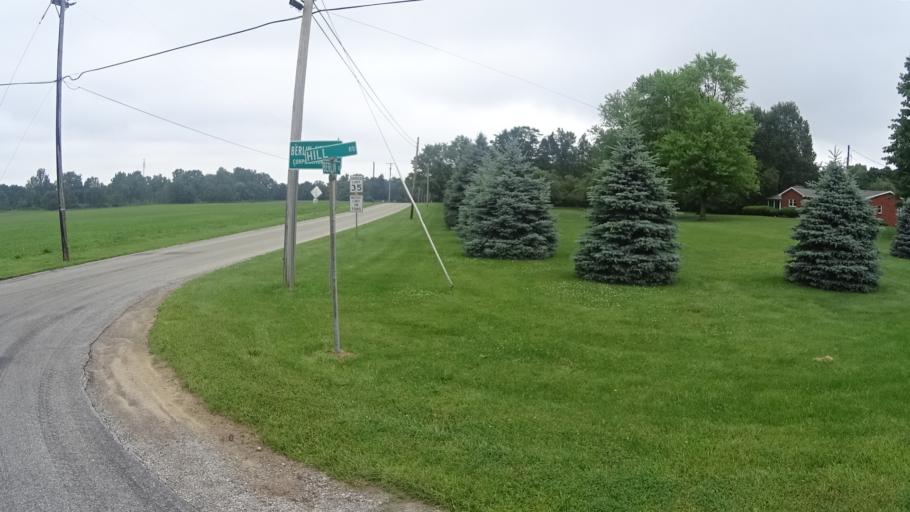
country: US
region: Ohio
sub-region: Erie County
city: Huron
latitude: 41.3157
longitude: -82.5001
